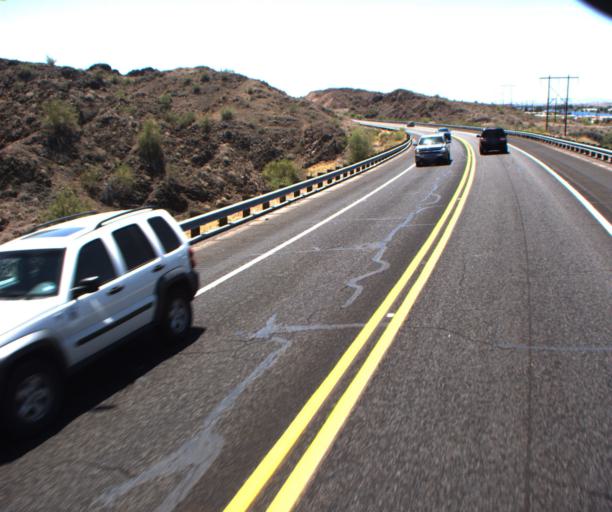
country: US
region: Arizona
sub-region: La Paz County
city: Cienega Springs
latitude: 34.2403
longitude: -114.1748
